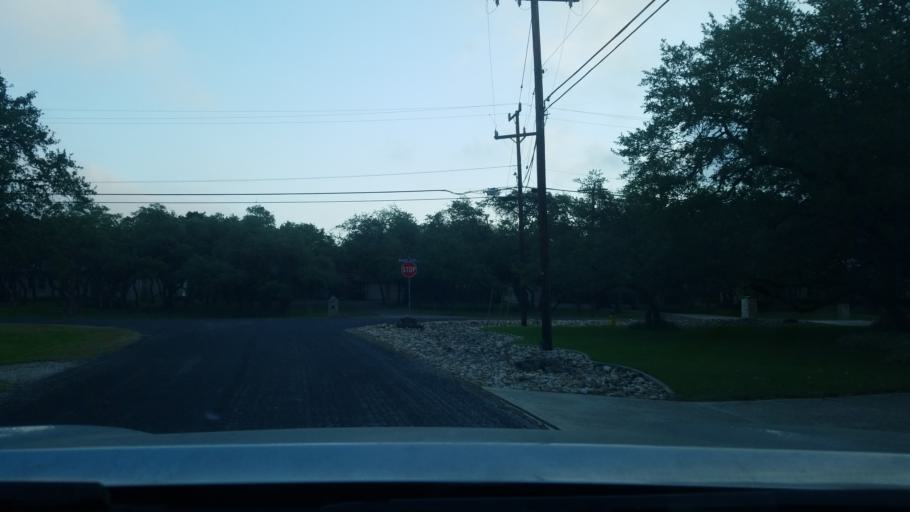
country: US
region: Texas
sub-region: Bexar County
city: Timberwood Park
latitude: 29.6987
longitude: -98.5029
